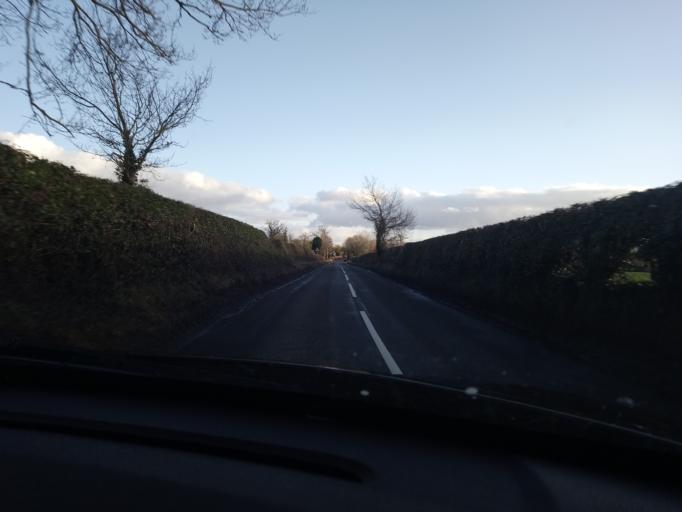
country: GB
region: England
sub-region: Shropshire
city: Petton
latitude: 52.8776
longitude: -2.7842
